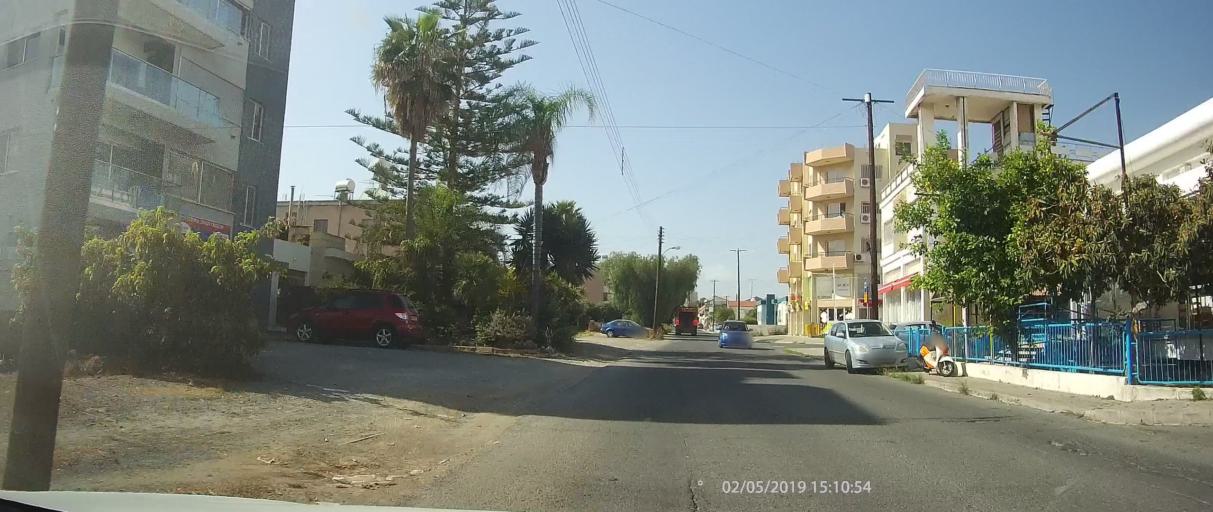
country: CY
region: Limassol
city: Limassol
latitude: 34.6707
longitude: 33.0229
